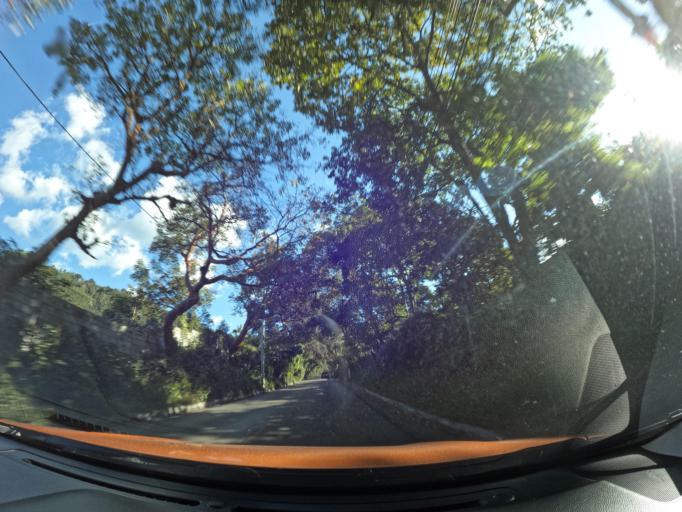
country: GT
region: Sacatepequez
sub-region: Municipio de Santa Maria de Jesus
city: Santa Maria de Jesus
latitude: 14.5266
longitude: -90.7260
